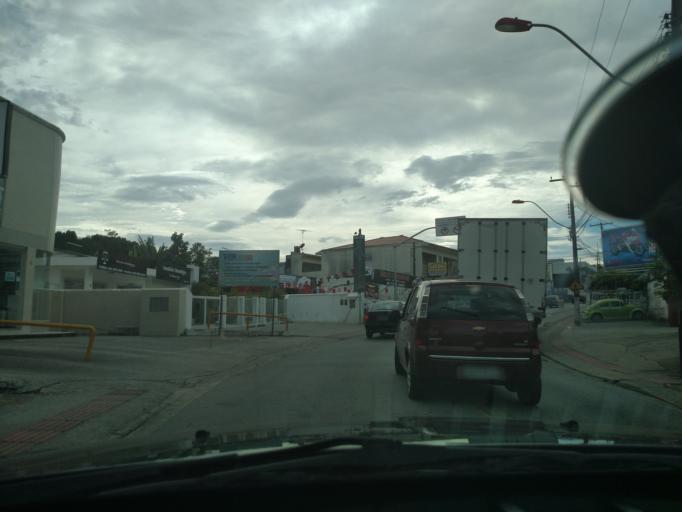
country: BR
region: Santa Catarina
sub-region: Sao Jose
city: Campinas
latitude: -27.6058
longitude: -48.6369
